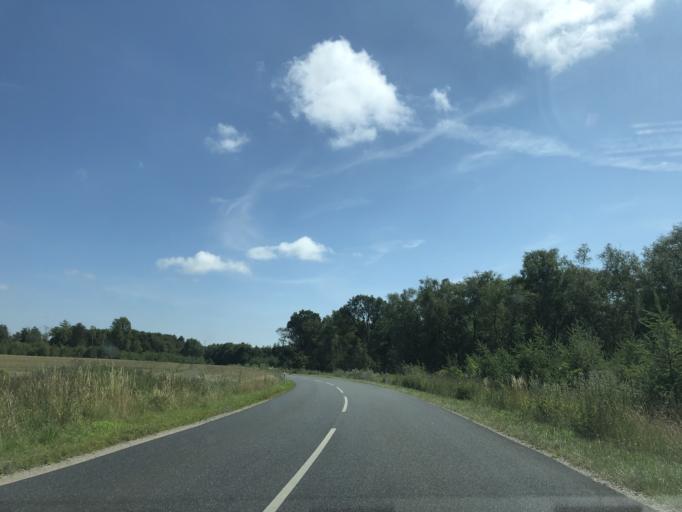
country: DK
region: Central Jutland
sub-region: Favrskov Kommune
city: Ulstrup
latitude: 56.3049
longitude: 9.7659
